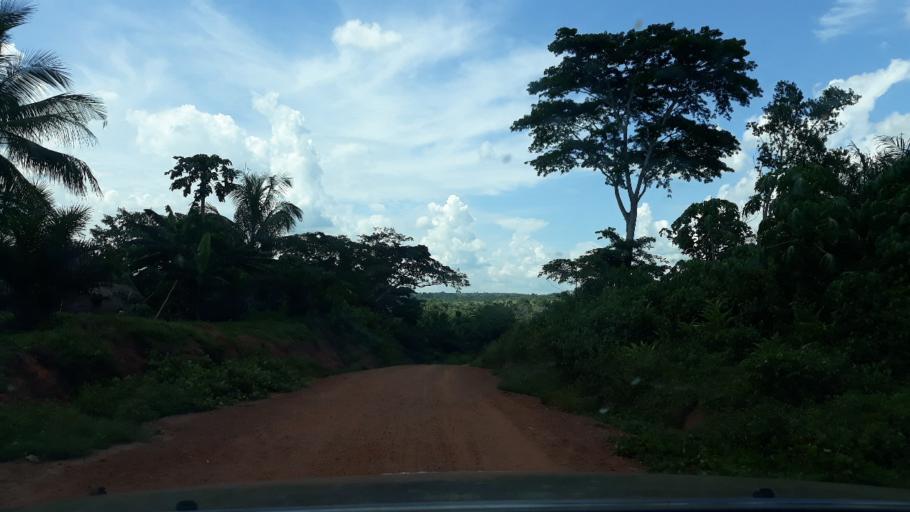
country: CD
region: Equateur
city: Businga
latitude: 3.4023
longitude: 20.3808
